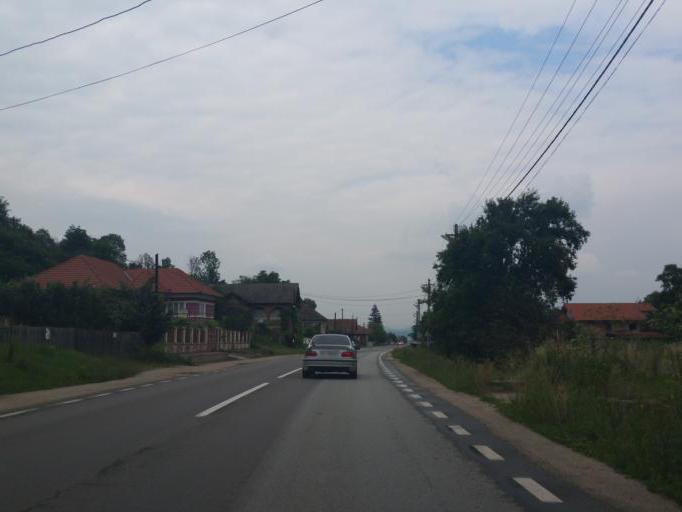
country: RO
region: Salaj
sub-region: Comuna Zimbor
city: Zimbor
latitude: 47.0027
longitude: 23.2564
